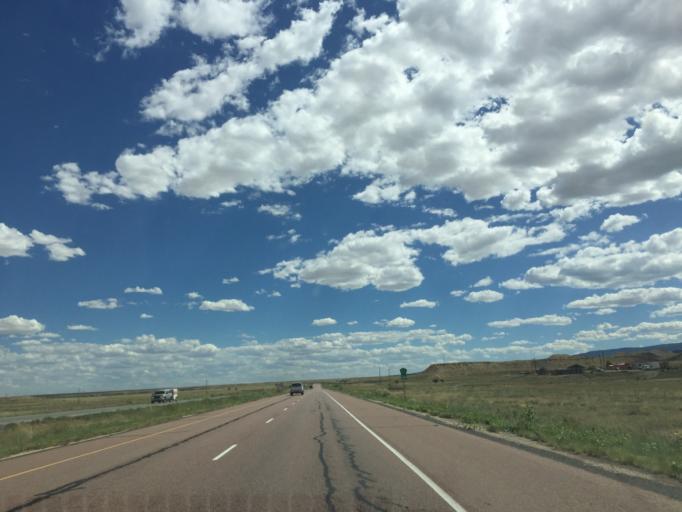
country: US
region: New Mexico
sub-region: McKinley County
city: Navajo
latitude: 36.1625
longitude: -108.7115
